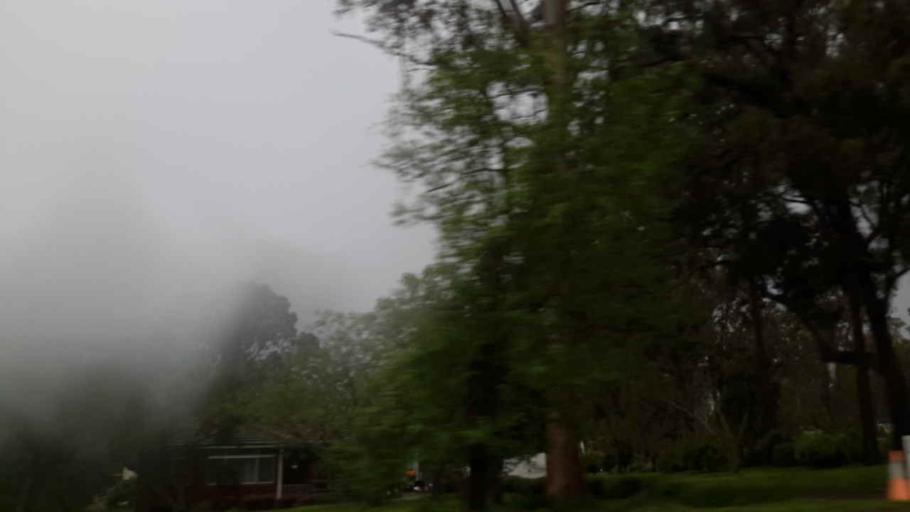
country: AU
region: New South Wales
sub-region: Wollondilly
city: Douglas Park
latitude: -34.2098
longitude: 150.7199
